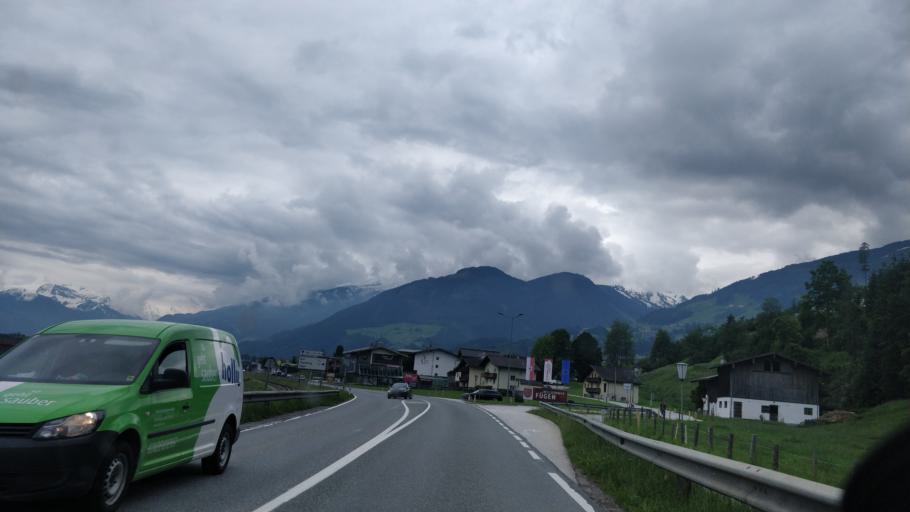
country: AT
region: Tyrol
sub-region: Politischer Bezirk Schwaz
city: Fugen
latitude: 47.3545
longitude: 11.8515
